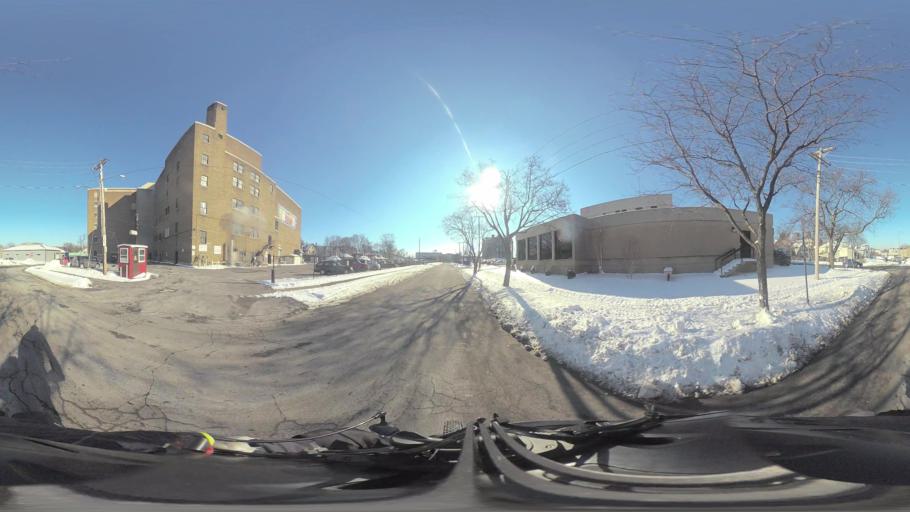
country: US
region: New York
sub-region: Monroe County
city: Rochester
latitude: 43.1599
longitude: -77.5889
